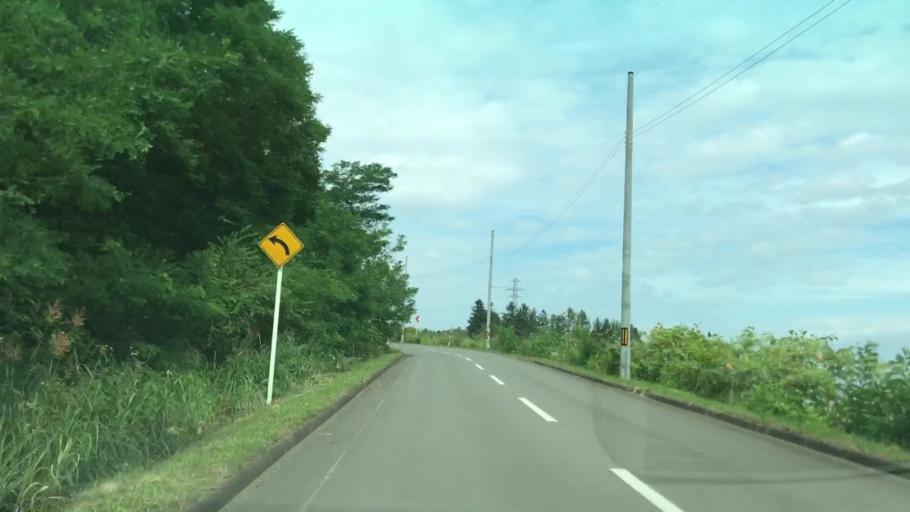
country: JP
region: Hokkaido
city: Yoichi
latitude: 43.1780
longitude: 140.8427
